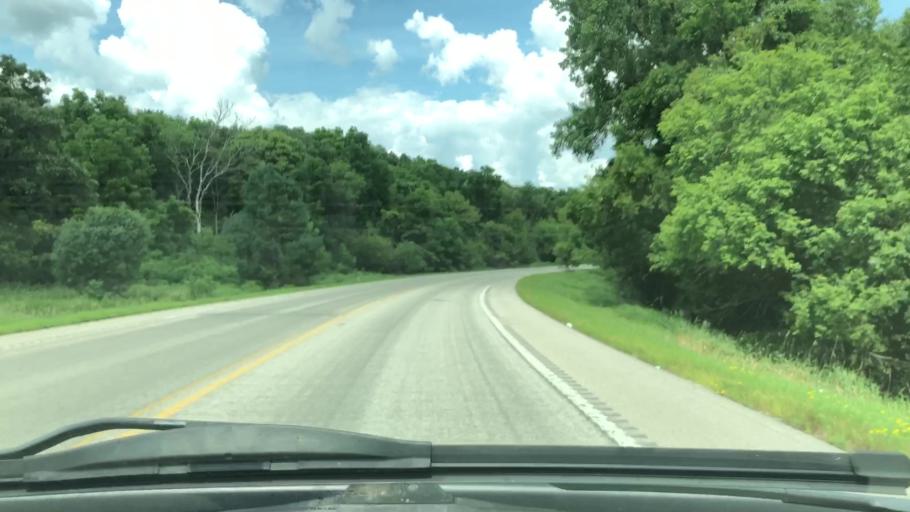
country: US
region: Minnesota
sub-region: Olmsted County
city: Rochester
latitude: 43.9814
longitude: -92.5095
